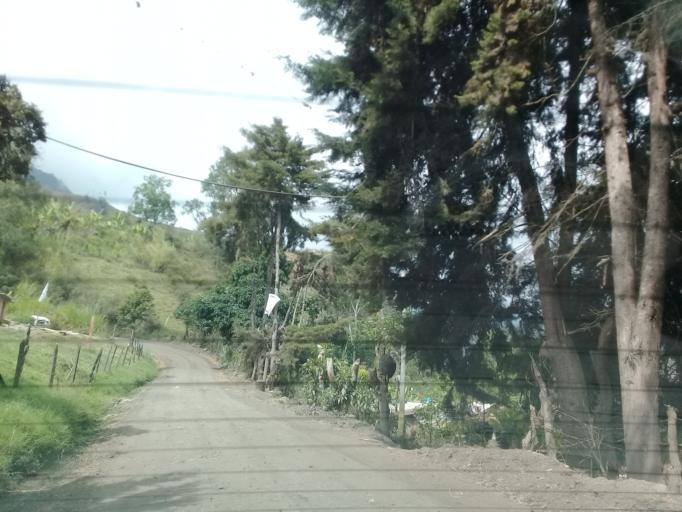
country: CO
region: Cundinamarca
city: Caqueza
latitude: 4.4137
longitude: -73.9850
